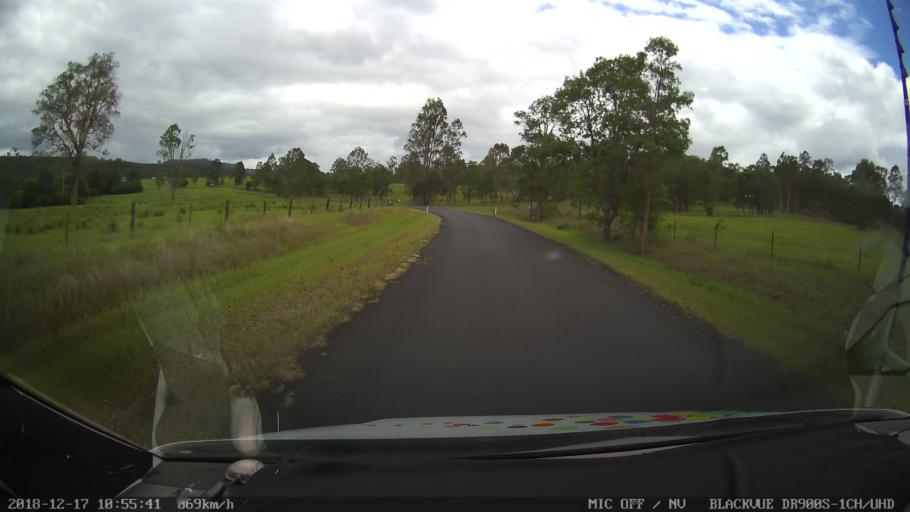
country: AU
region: New South Wales
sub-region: Richmond Valley
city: Casino
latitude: -28.8271
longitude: 152.5821
